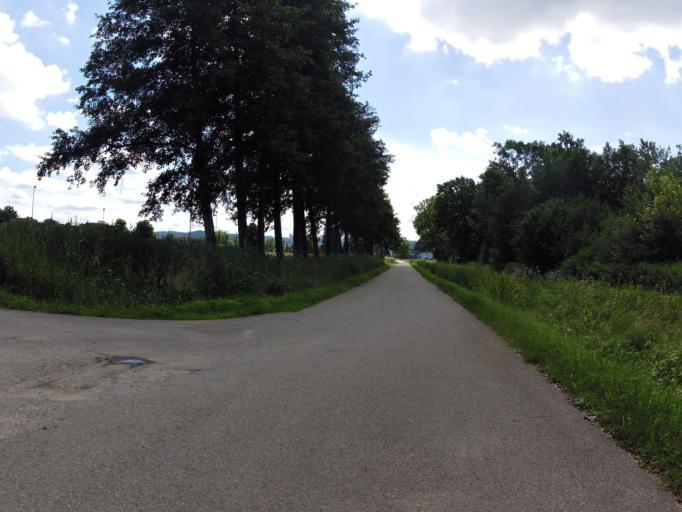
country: DE
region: Baden-Wuerttemberg
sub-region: Freiburg Region
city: Kippenheim
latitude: 48.3325
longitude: 7.8120
